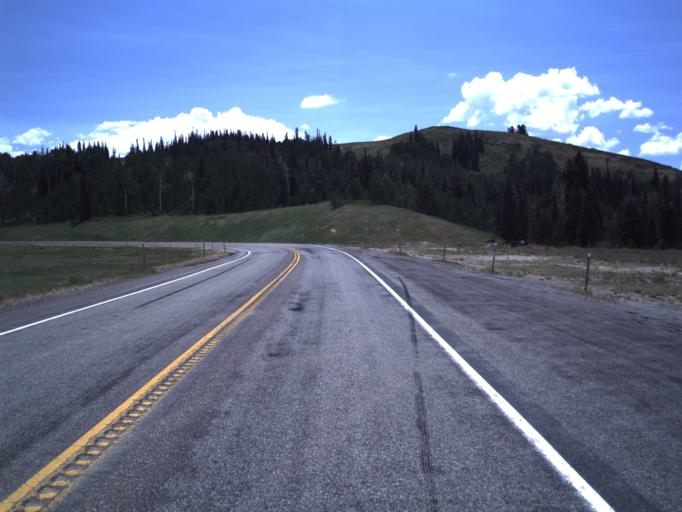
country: US
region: Utah
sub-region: Sanpete County
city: Fairview
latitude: 39.6380
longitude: -111.3298
